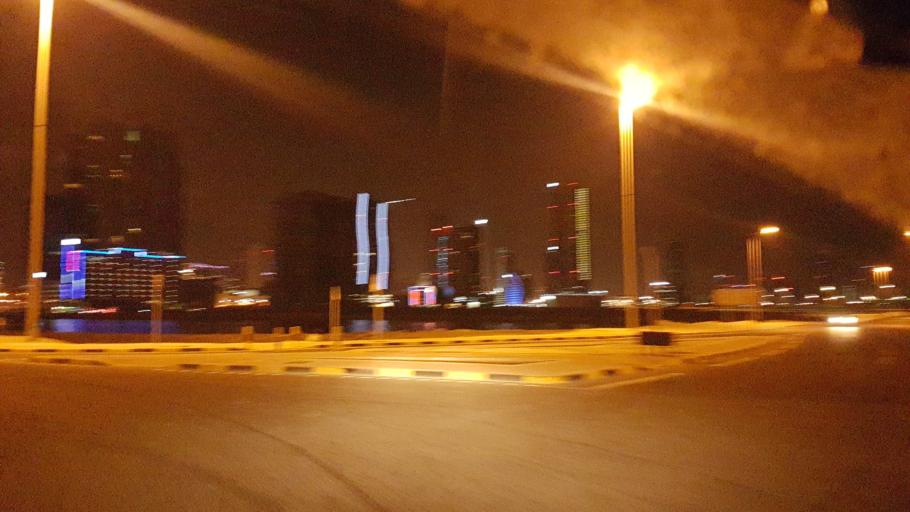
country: BH
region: Manama
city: Jidd Hafs
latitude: 26.2411
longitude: 50.5594
